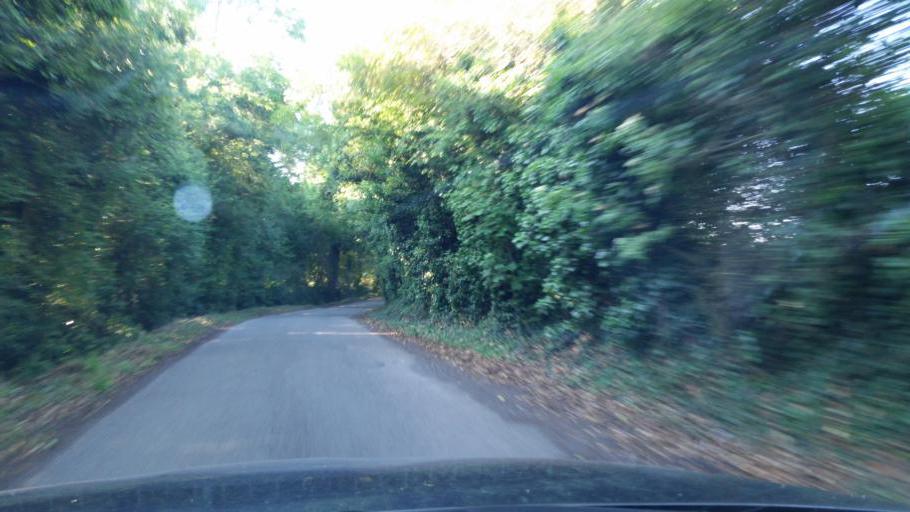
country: IE
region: Leinster
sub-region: Dublin City
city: Finglas
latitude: 53.4597
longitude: -6.3243
